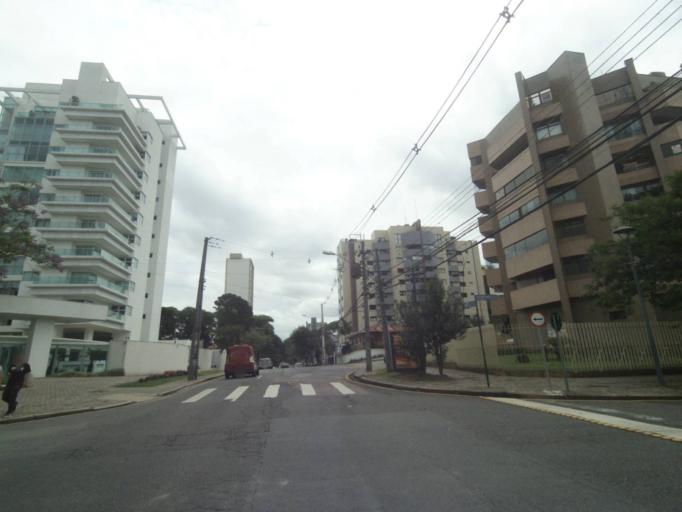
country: BR
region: Parana
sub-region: Curitiba
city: Curitiba
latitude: -25.4328
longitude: -49.2867
